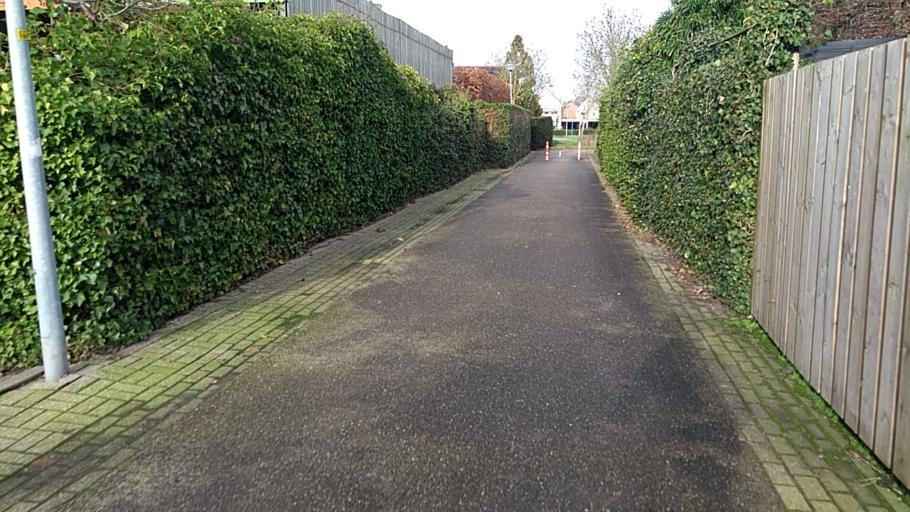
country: NL
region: Overijssel
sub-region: Gemeente Almelo
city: Almelo
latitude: 52.3751
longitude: 6.6824
